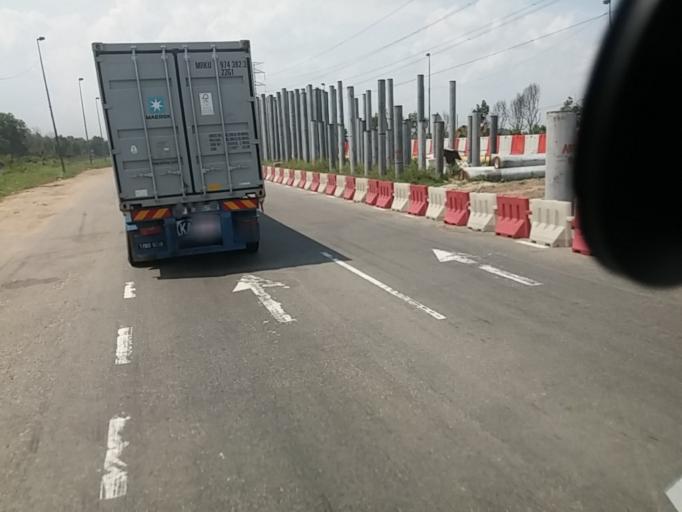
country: MY
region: Selangor
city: Klang
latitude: 2.9709
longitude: 101.3643
